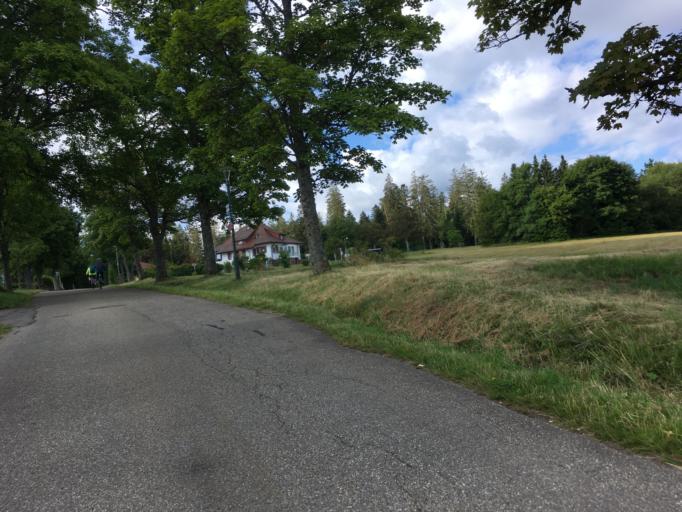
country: DE
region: Baden-Wuerttemberg
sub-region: Karlsruhe Region
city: Freudenstadt
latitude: 48.4547
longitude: 8.4094
